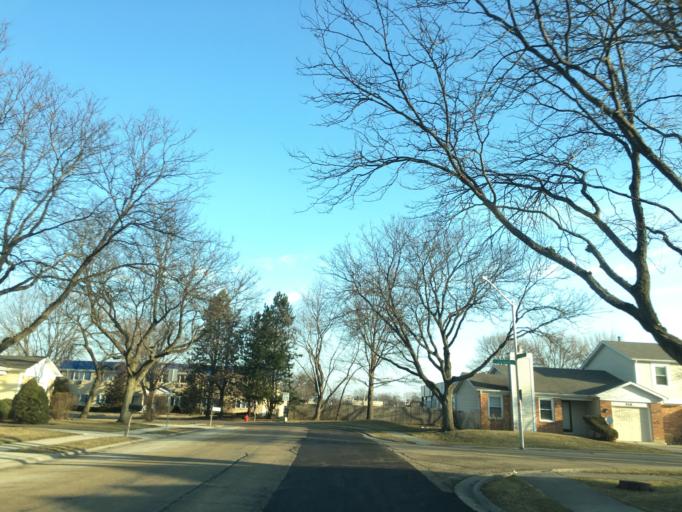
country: US
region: Illinois
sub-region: Cook County
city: Hoffman Estates
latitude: 42.0463
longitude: -88.1032
